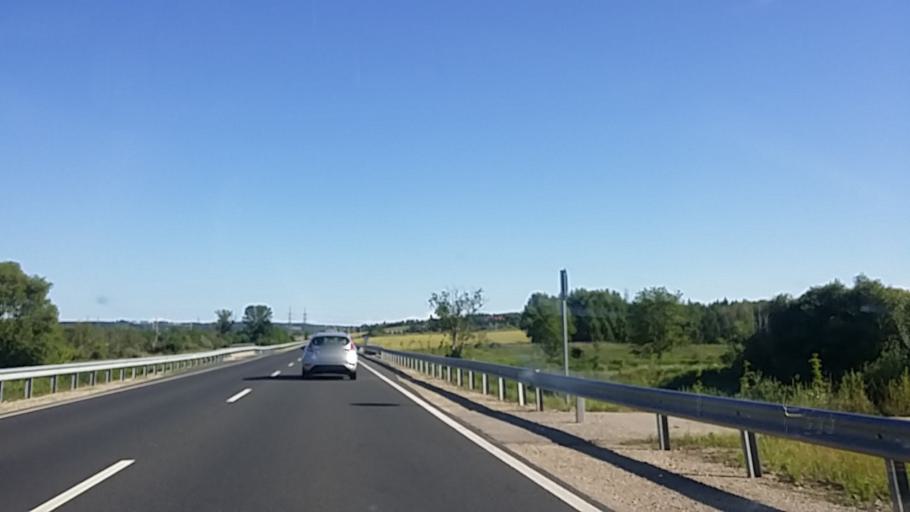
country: HU
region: Zala
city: Heviz
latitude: 46.7686
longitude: 17.1855
